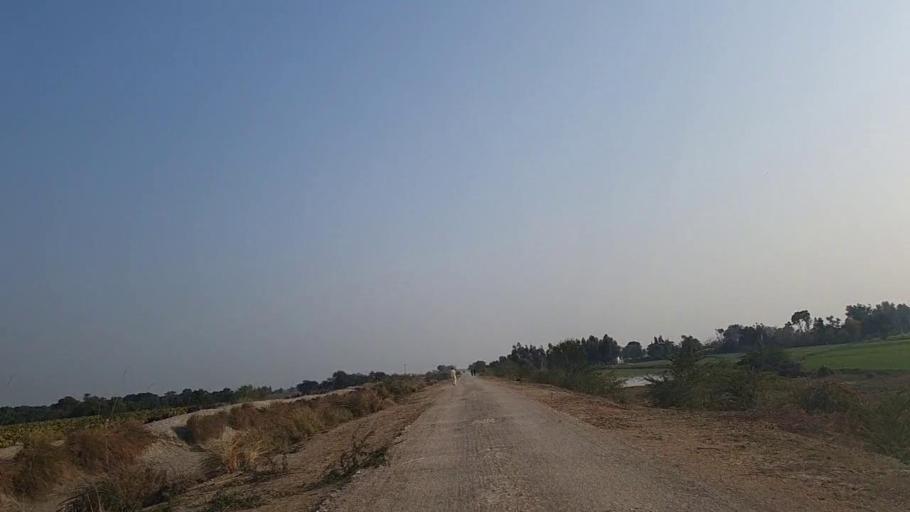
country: PK
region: Sindh
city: Jam Sahib
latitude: 26.2330
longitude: 68.5943
